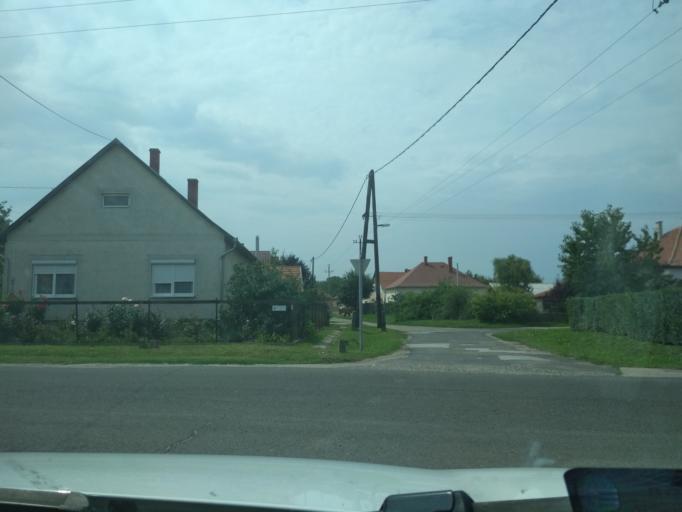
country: HU
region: Jasz-Nagykun-Szolnok
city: Tiszafured
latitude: 47.6110
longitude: 20.7677
